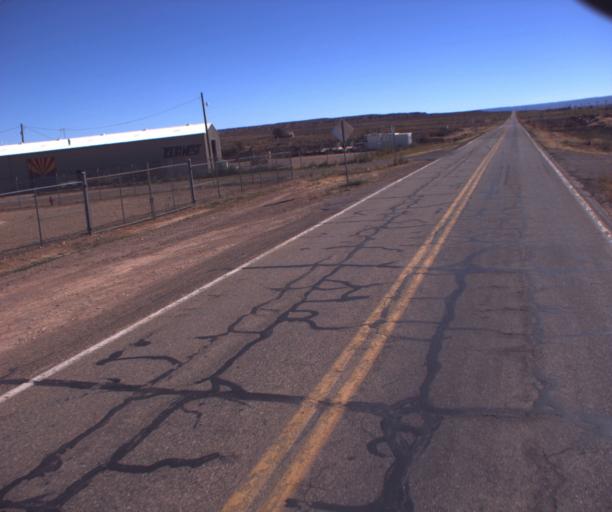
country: US
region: Arizona
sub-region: Coconino County
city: Fredonia
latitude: 36.9395
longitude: -112.5211
